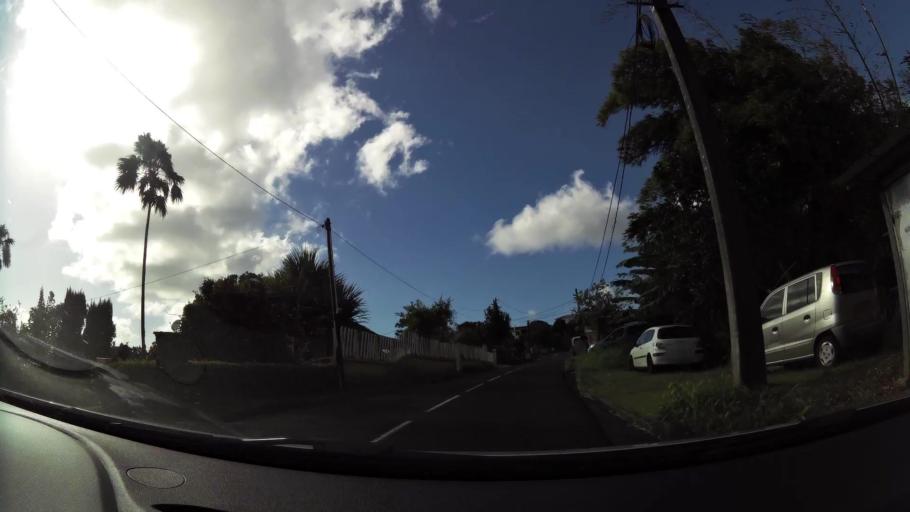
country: MQ
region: Martinique
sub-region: Martinique
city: Fort-de-France
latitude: 14.6499
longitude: -61.0847
